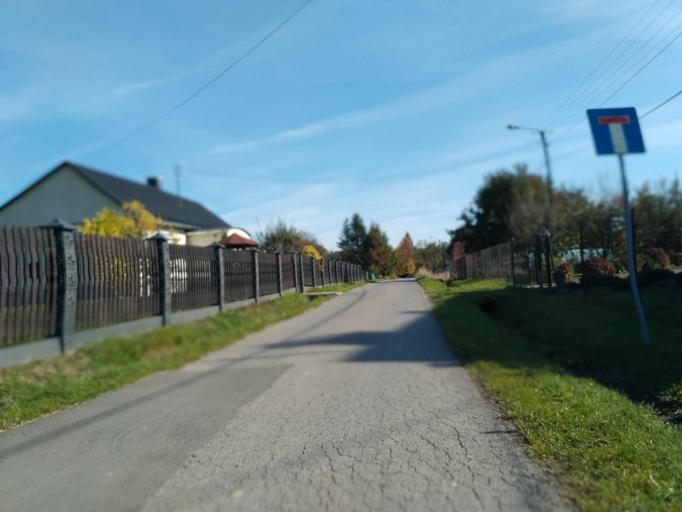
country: PL
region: Subcarpathian Voivodeship
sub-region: Powiat rzeszowski
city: Trzciana
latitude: 50.0879
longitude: 21.8140
